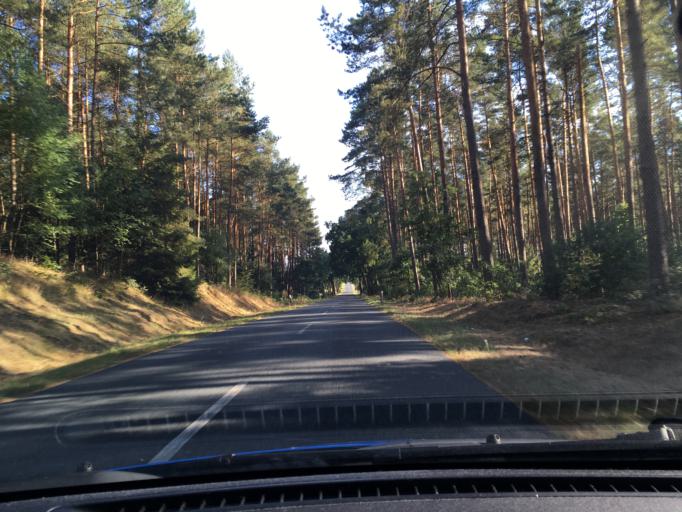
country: DE
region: Lower Saxony
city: Thomasburg
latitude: 53.2350
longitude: 10.7038
